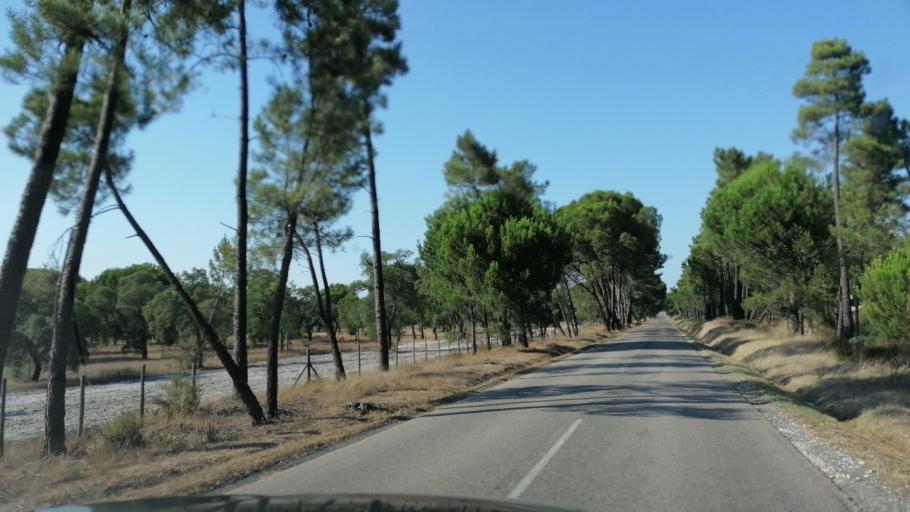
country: PT
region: Santarem
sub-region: Coruche
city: Coruche
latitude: 38.9051
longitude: -8.5275
